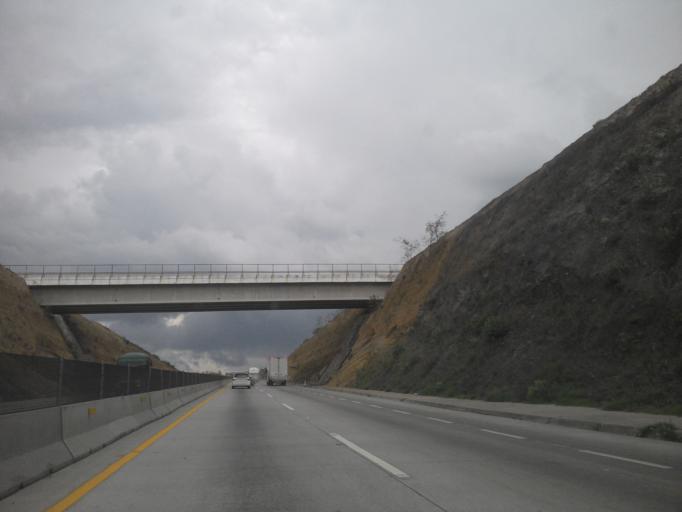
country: MX
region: Hidalgo
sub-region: San Agustin Tlaxiaca
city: Oriental de Zapata
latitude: 19.9636
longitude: -99.0237
